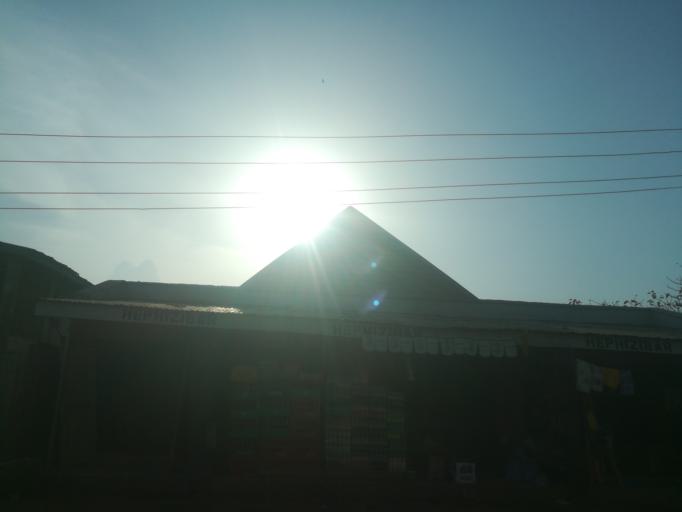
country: NG
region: Oyo
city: Moniya
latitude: 7.5689
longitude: 3.8856
